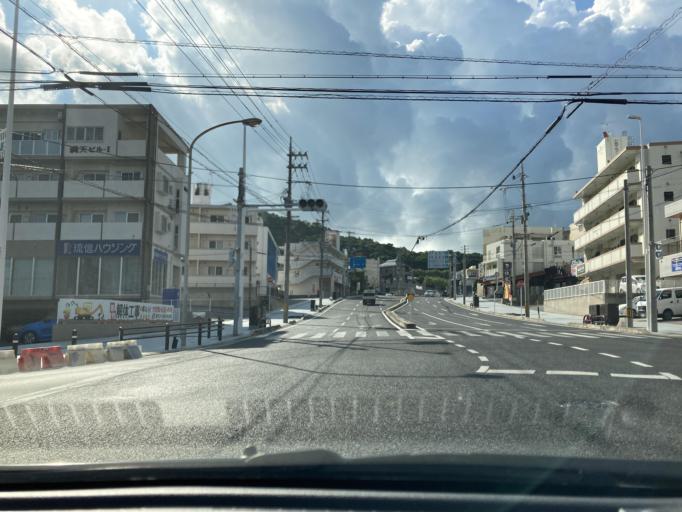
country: JP
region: Okinawa
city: Tomigusuku
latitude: 26.1909
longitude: 127.7296
